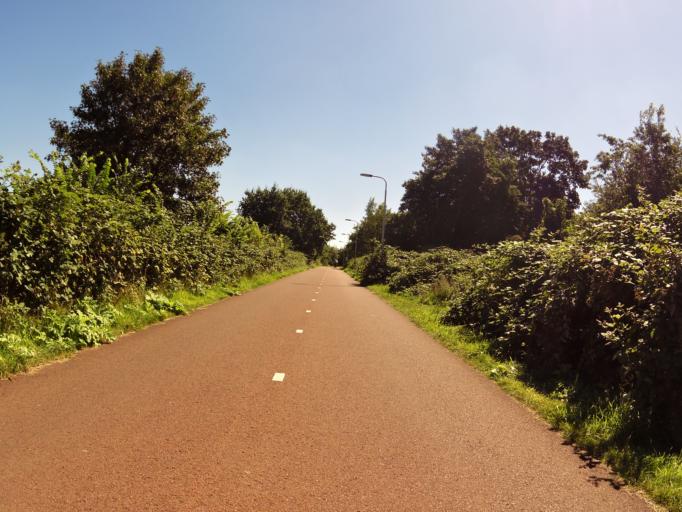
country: NL
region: Gelderland
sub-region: Gemeente Nijmegen
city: Nijmegen
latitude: 51.8312
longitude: 5.8605
